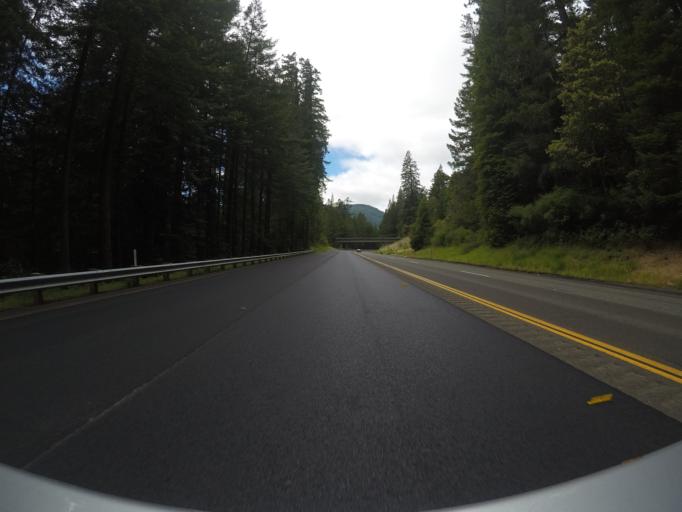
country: US
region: California
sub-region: Humboldt County
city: Redway
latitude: 40.3052
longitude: -123.8989
